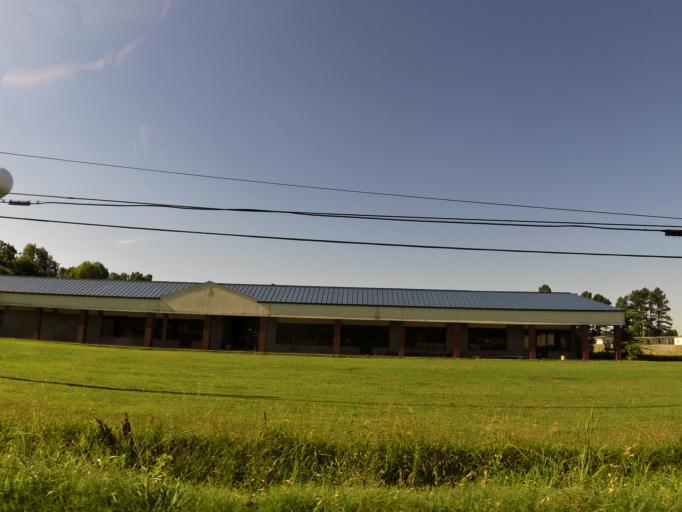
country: US
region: Arkansas
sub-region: Clay County
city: Corning
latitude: 36.4114
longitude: -90.5964
